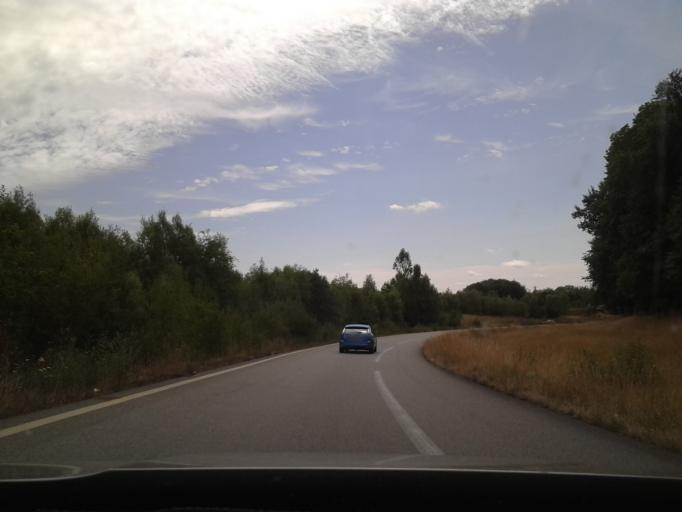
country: FR
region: Pays de la Loire
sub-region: Departement de la Sarthe
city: Champagne
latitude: 48.0500
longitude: 0.2904
